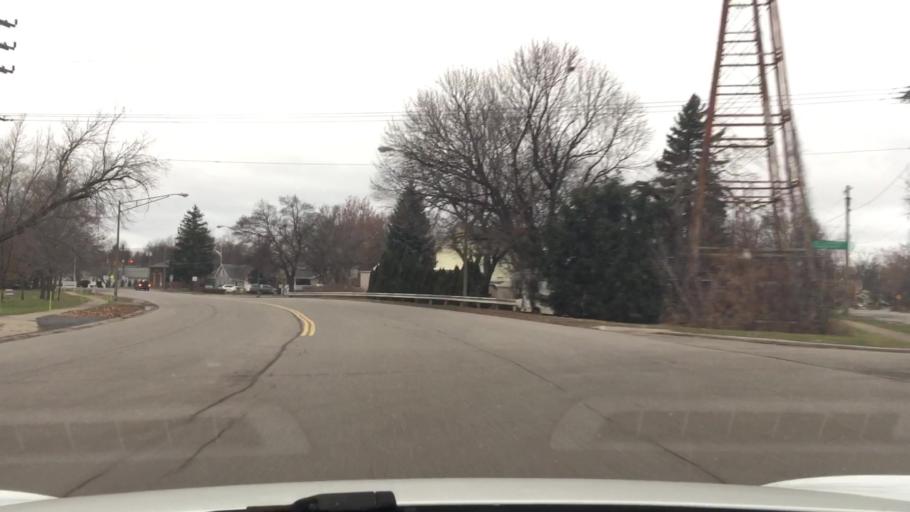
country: US
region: New York
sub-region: Erie County
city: Tonawanda
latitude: 43.0121
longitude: -78.8635
